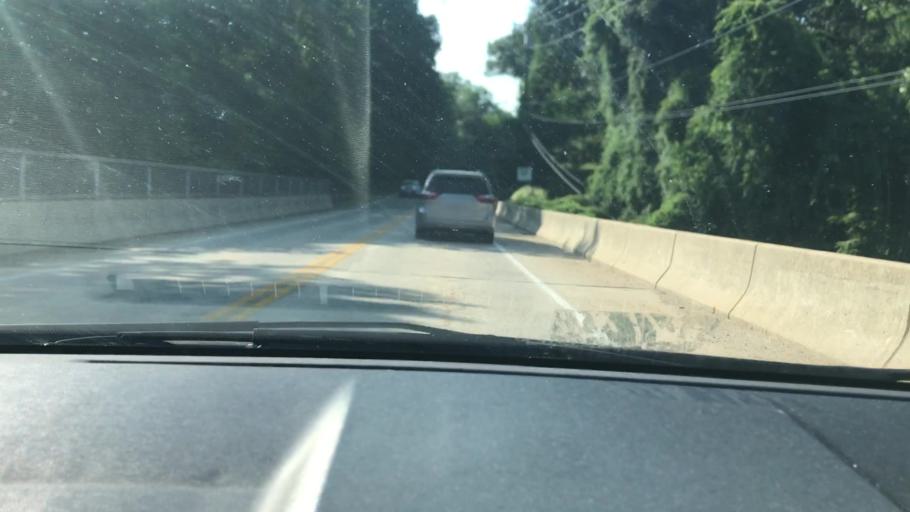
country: US
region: Virginia
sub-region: Fairfax County
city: Great Falls
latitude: 38.9755
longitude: -77.2553
